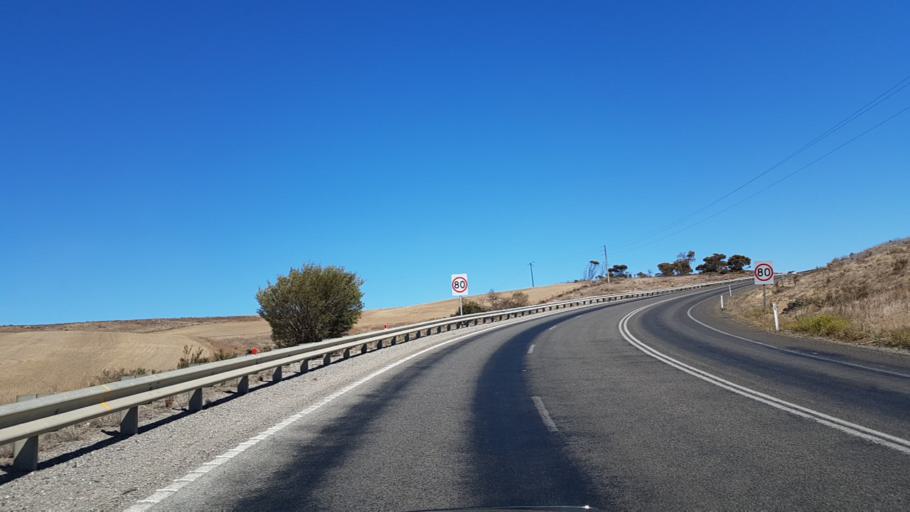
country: AU
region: South Australia
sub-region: Copper Coast
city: Kadina
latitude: -34.0675
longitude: 138.0605
